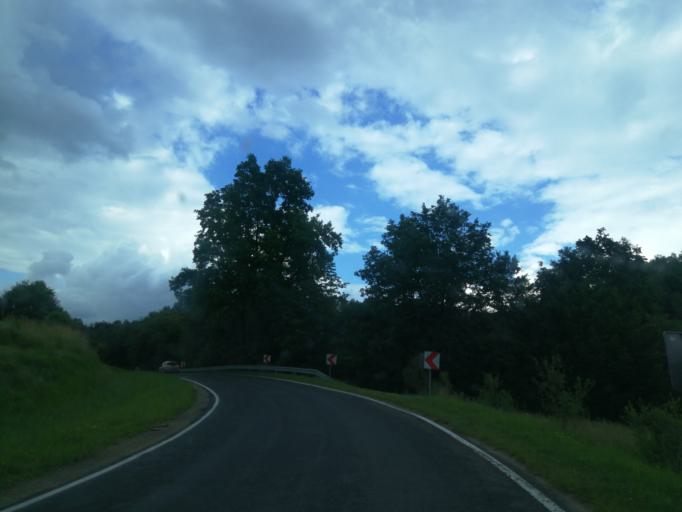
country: PL
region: Subcarpathian Voivodeship
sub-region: Powiat leski
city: Olszanica
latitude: 49.4282
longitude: 22.4570
